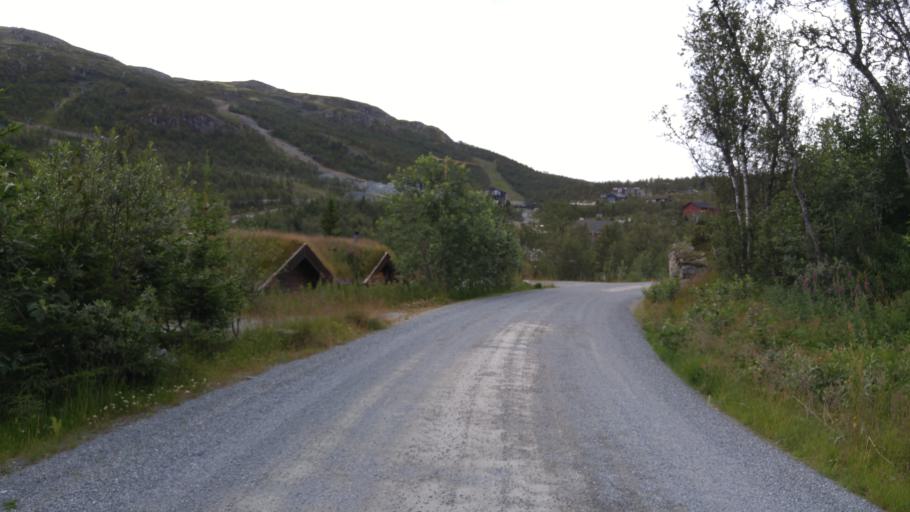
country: NO
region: Buskerud
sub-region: Hemsedal
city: Hemsedal
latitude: 60.8574
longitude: 8.4931
